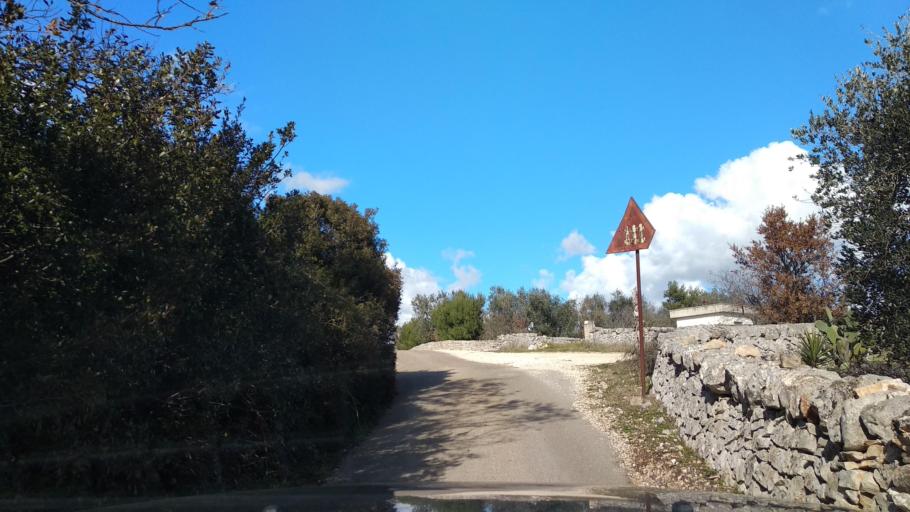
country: IT
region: Apulia
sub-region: Provincia di Brindisi
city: Casalini
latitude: 40.7137
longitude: 17.4525
